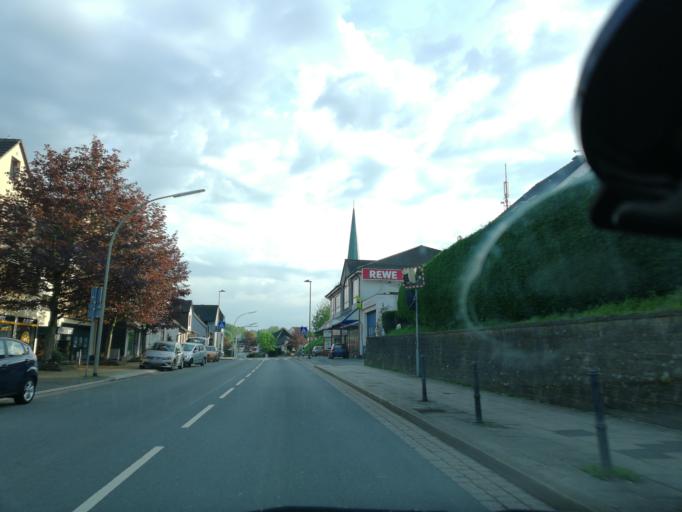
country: DE
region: North Rhine-Westphalia
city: Wetter (Ruhr)
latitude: 51.3747
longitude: 7.3707
